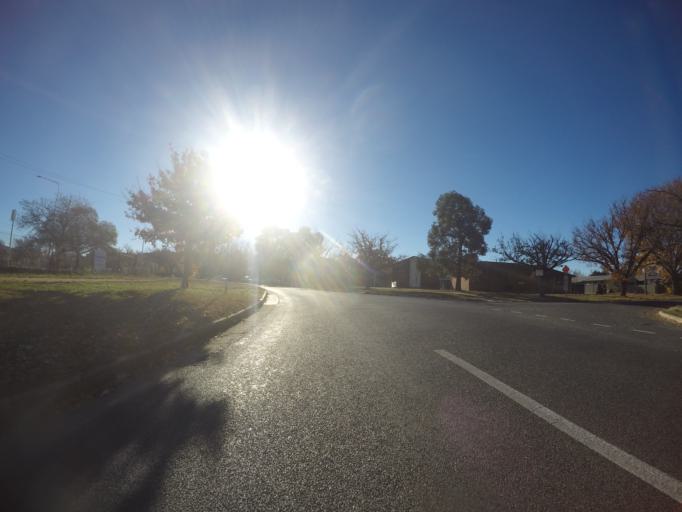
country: AU
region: Australian Capital Territory
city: Canberra
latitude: -35.2741
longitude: 149.1362
